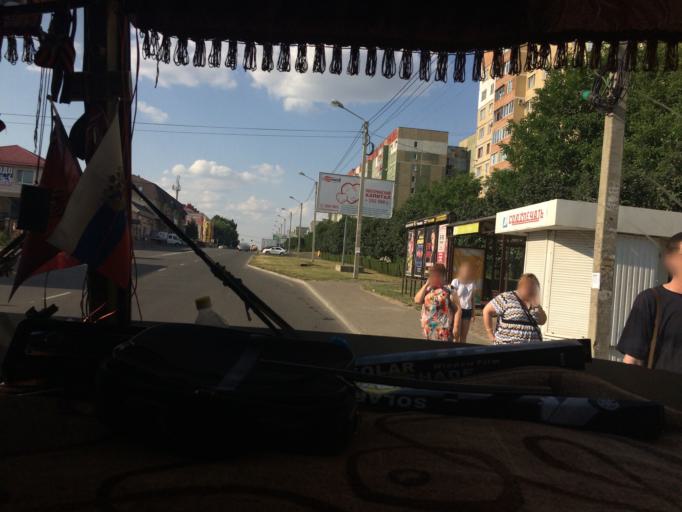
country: RU
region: Stavropol'skiy
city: Tatarka
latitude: 45.0041
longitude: 41.9117
